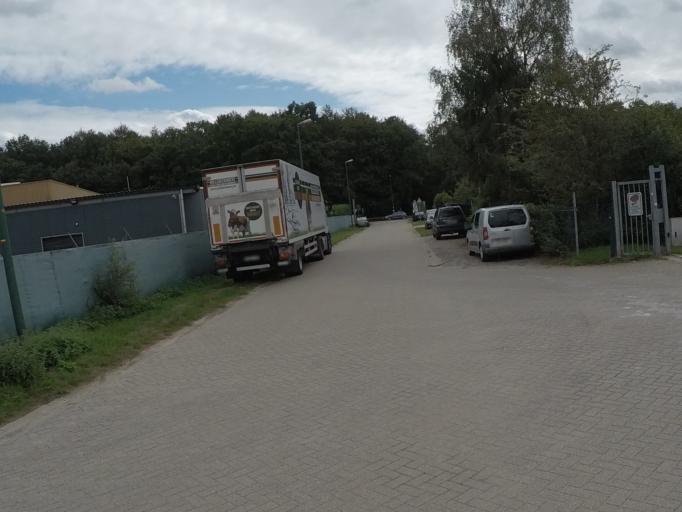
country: BE
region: Flanders
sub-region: Provincie Antwerpen
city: Vorselaar
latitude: 51.2159
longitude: 4.7721
